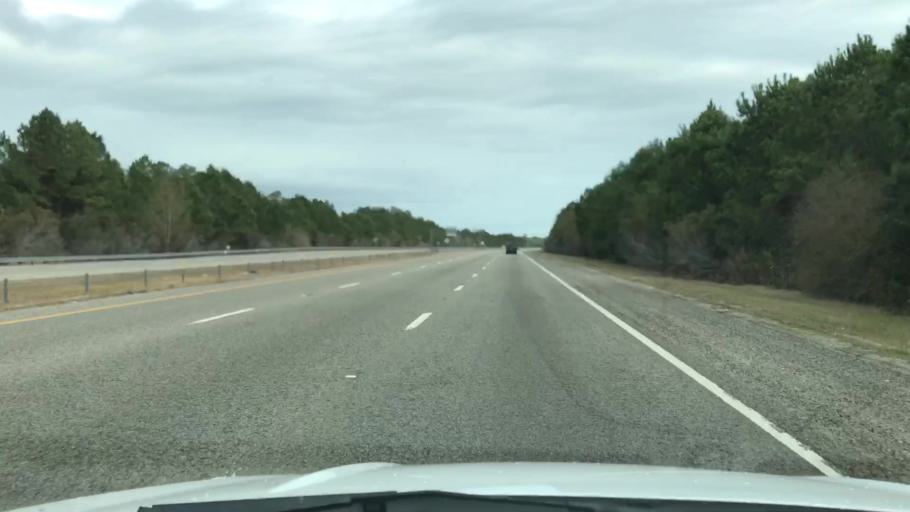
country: US
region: South Carolina
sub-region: Horry County
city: Socastee
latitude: 33.7179
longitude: -78.9999
